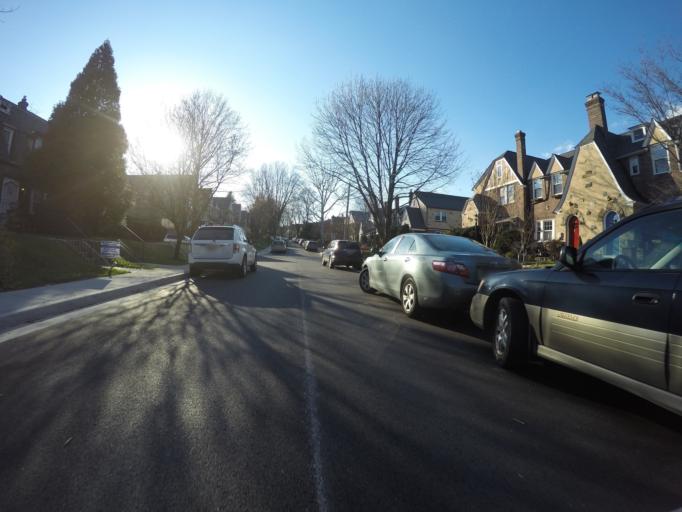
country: US
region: Maryland
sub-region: Baltimore County
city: Towson
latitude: 39.3762
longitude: -76.6102
